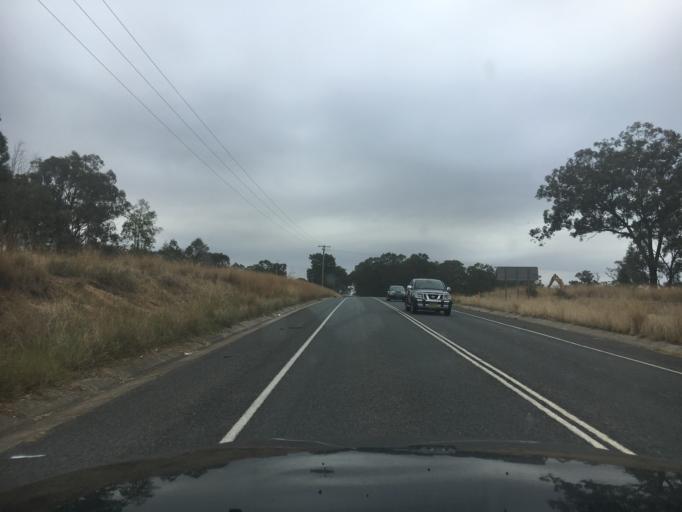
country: AU
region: New South Wales
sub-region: Singleton
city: Singleton
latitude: -32.5591
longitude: 151.1987
